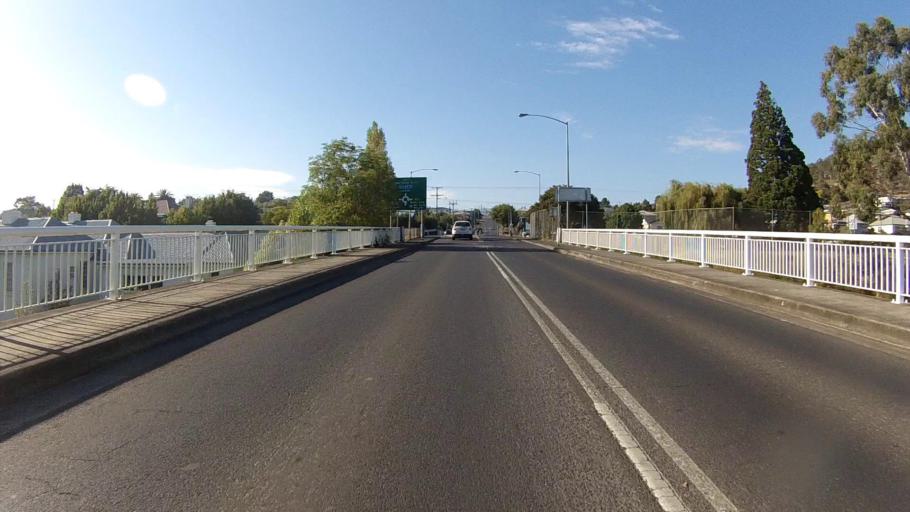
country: AU
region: Tasmania
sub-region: Derwent Valley
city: New Norfolk
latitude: -42.7795
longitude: 147.0570
